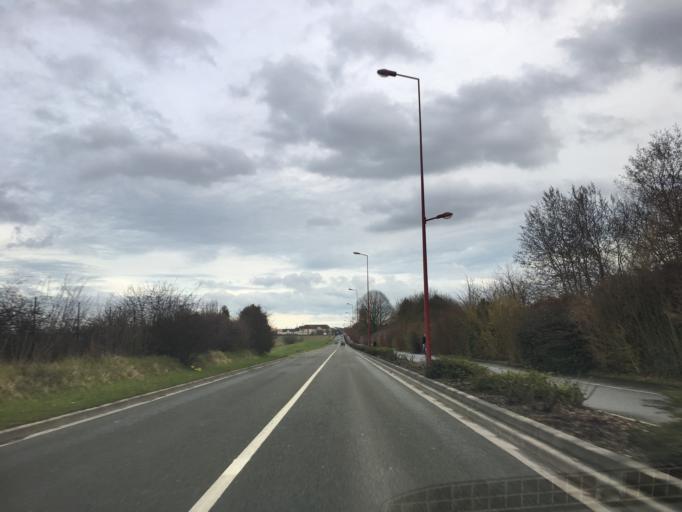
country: FR
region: Ile-de-France
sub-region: Departement du Val-d'Oise
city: Gonesse
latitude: 48.9979
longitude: 2.4354
